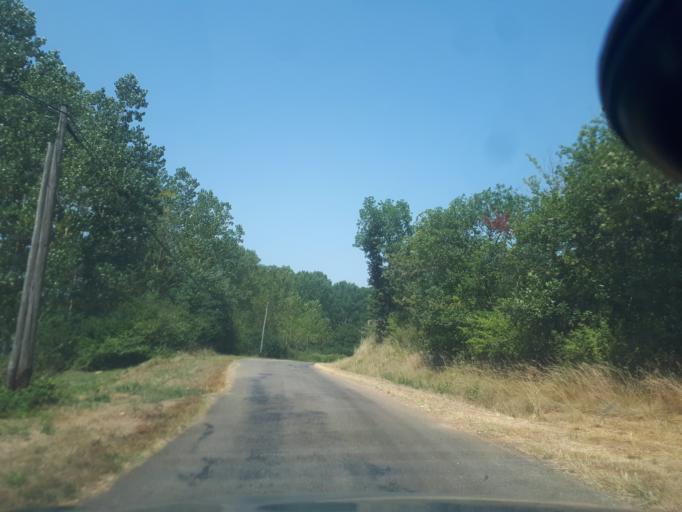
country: FR
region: Midi-Pyrenees
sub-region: Departement du Lot
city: Salviac
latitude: 44.7352
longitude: 1.2813
